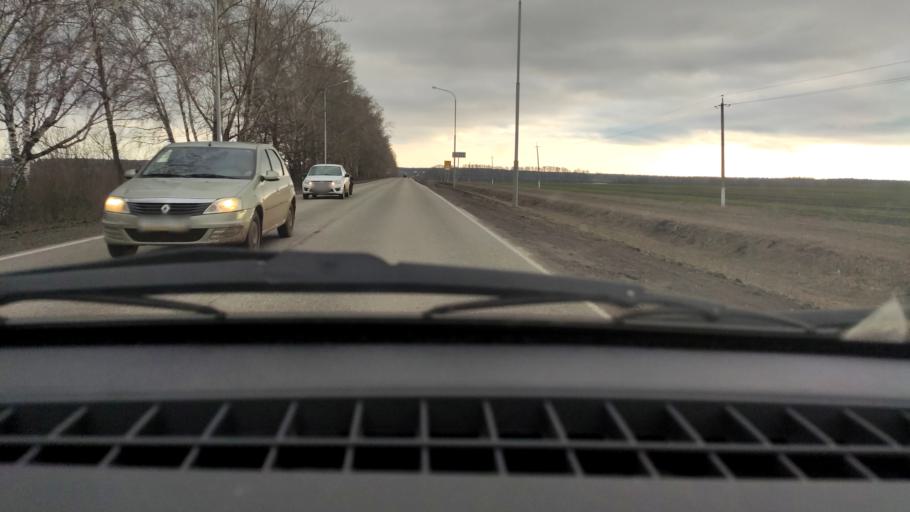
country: RU
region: Bashkortostan
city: Chishmy
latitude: 54.6615
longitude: 55.3953
